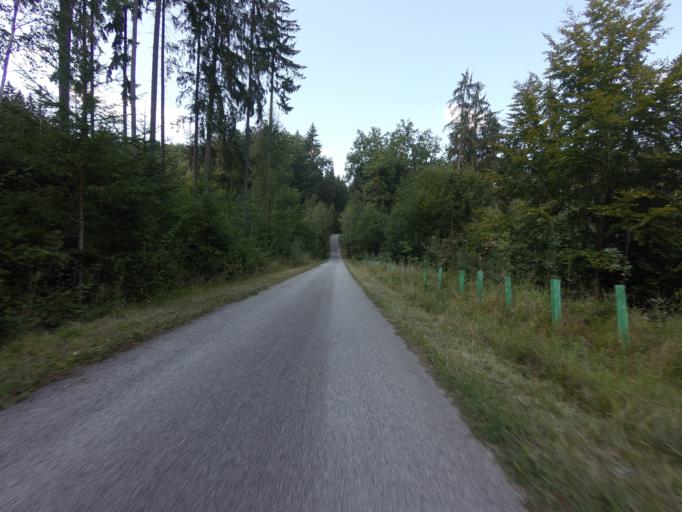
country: CZ
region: Jihocesky
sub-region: Okres Ceske Budejovice
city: Hluboka nad Vltavou
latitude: 49.1065
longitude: 14.4603
